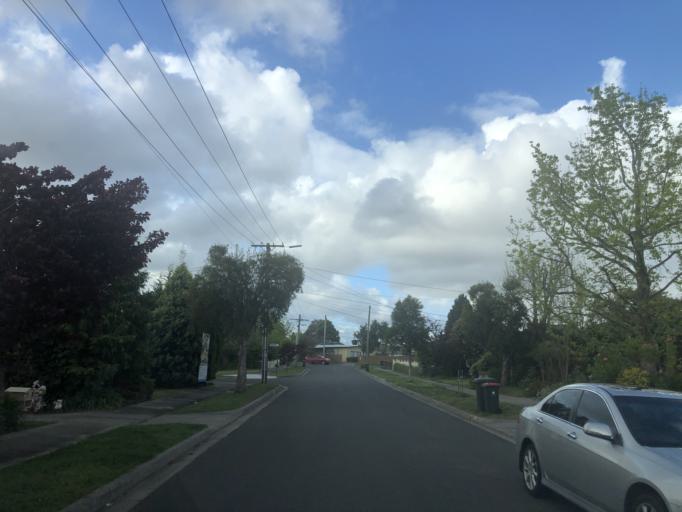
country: AU
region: Victoria
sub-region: Monash
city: Notting Hill
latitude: -37.8863
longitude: 145.1260
